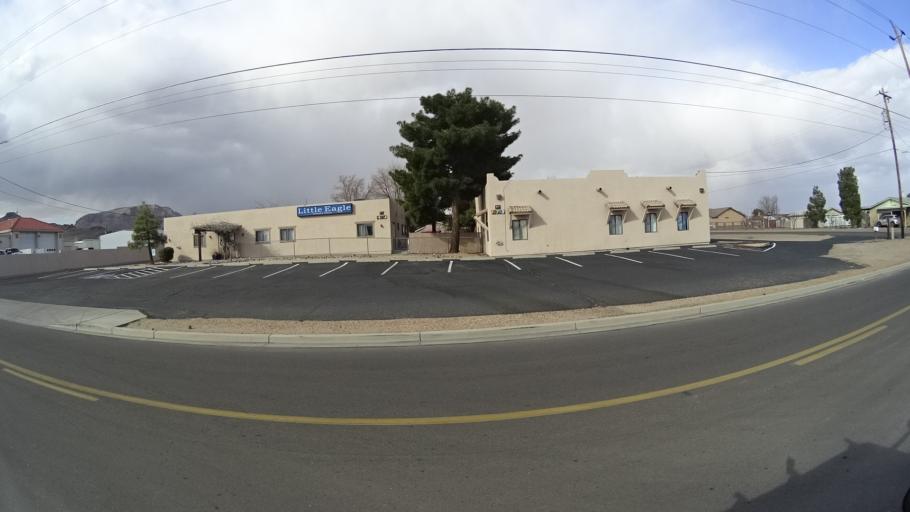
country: US
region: Arizona
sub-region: Mohave County
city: New Kingman-Butler
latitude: 35.2396
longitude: -114.0355
